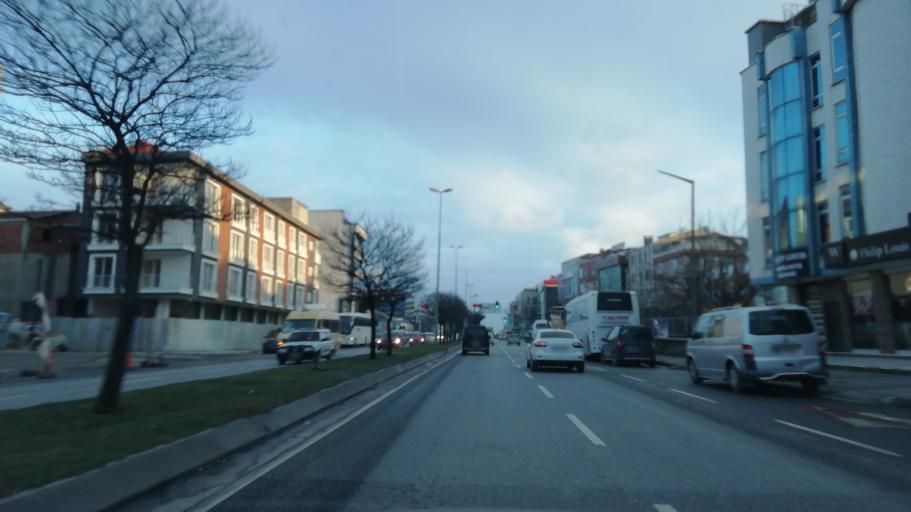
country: TR
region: Istanbul
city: Esenyurt
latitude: 41.0083
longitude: 28.7032
